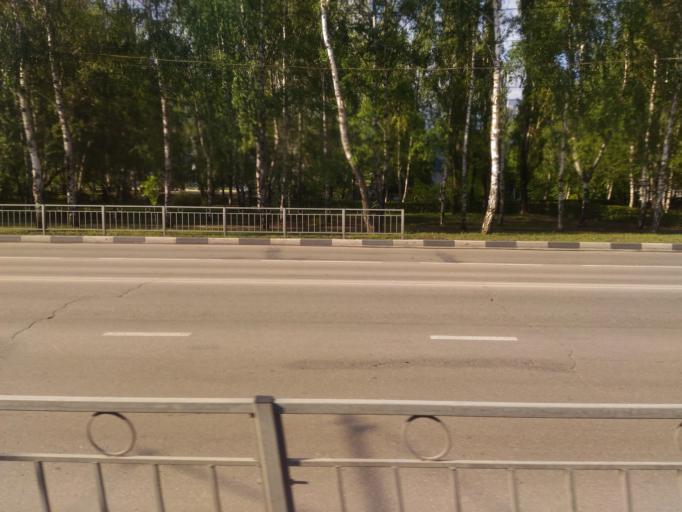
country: RU
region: Ulyanovsk
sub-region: Ulyanovskiy Rayon
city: Ulyanovsk
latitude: 54.3078
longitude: 48.3394
